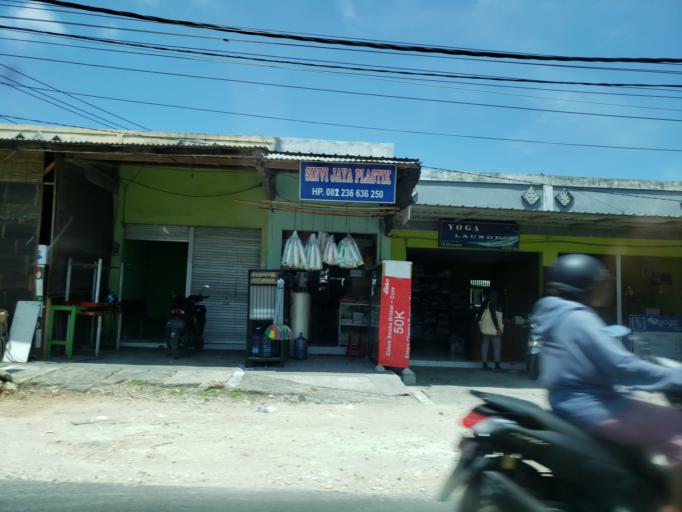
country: ID
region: Bali
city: Kangin
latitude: -8.8308
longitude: 115.1325
